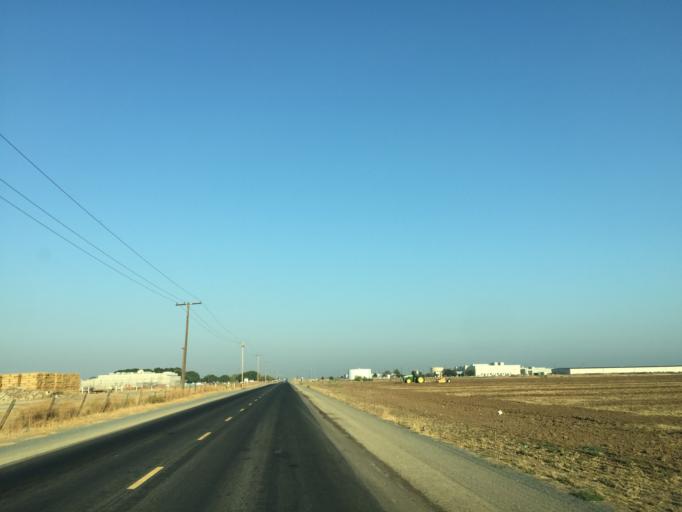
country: US
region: California
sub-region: Tulare County
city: Cutler
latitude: 36.4580
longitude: -119.3160
